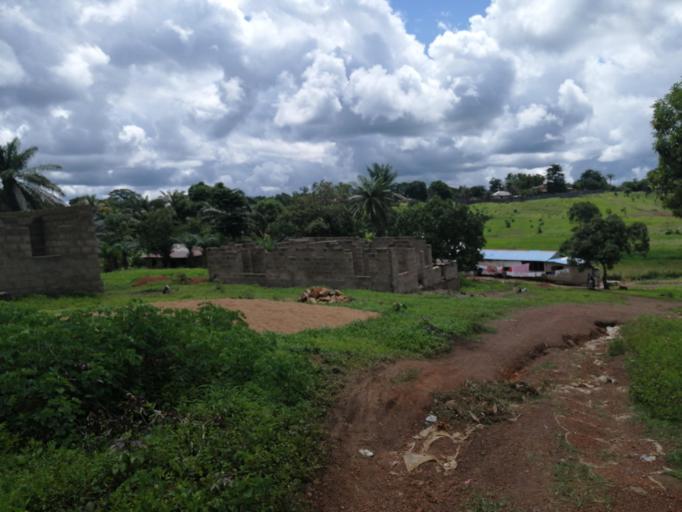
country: SL
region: Northern Province
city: Port Loko
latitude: 8.7724
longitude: -12.7803
